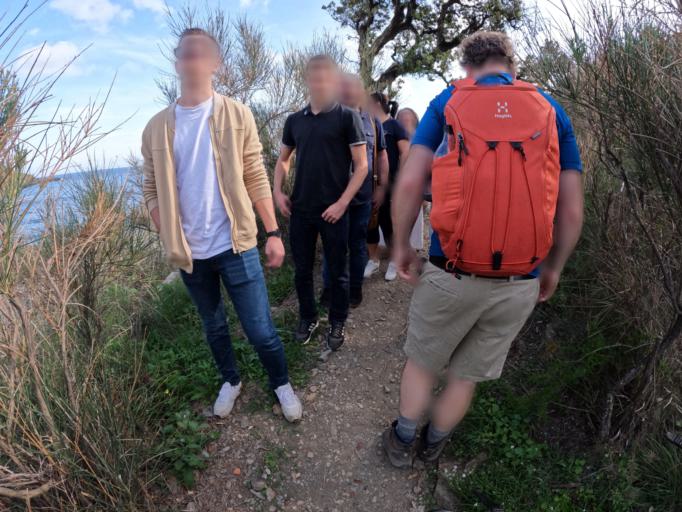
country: FR
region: Languedoc-Roussillon
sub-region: Departement des Pyrenees-Orientales
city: Cervera de la Marenda
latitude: 42.4596
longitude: 3.1567
